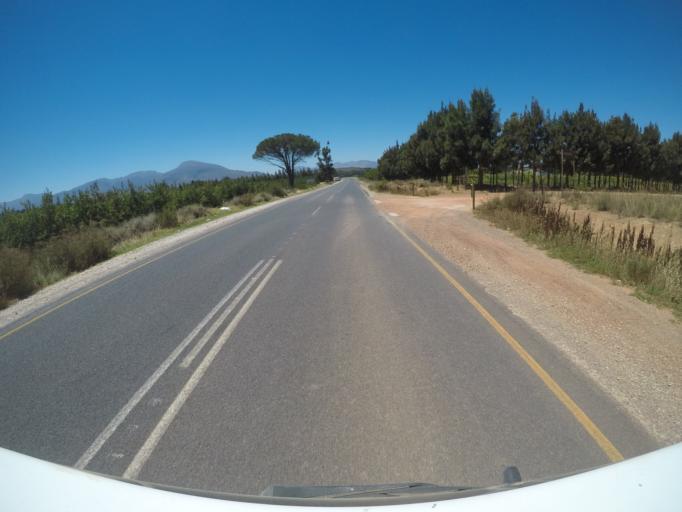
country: ZA
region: Western Cape
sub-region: Overberg District Municipality
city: Grabouw
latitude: -34.0584
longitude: 19.1394
